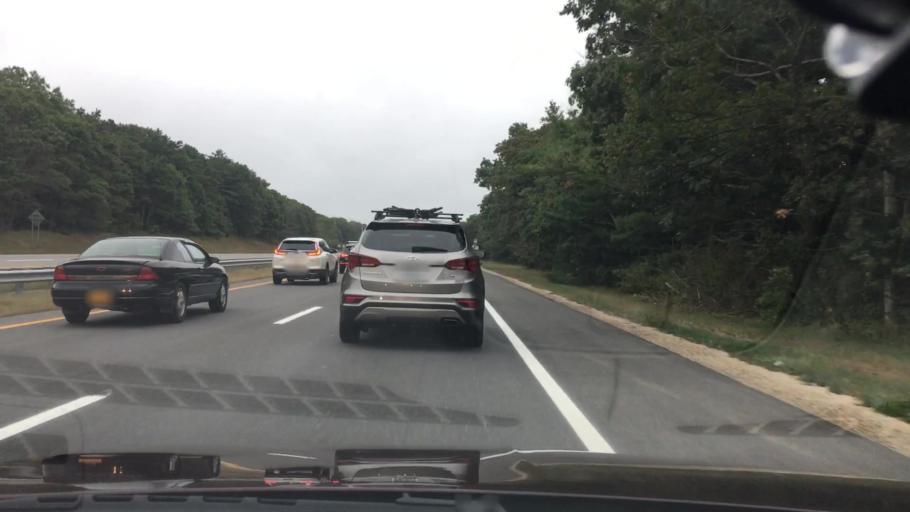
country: US
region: New York
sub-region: Suffolk County
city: Centereach
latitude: 40.8861
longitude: -73.1091
